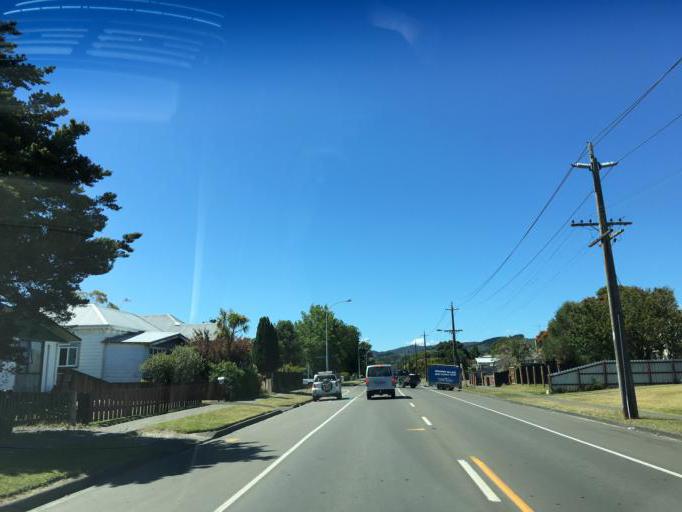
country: NZ
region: Gisborne
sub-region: Gisborne District
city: Gisborne
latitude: -38.6632
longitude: 178.0065
